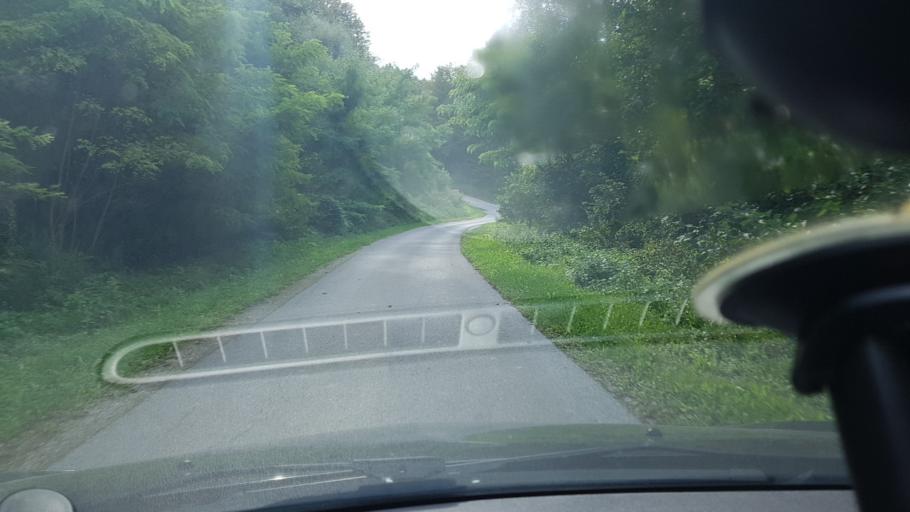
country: HR
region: Krapinsko-Zagorska
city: Radoboj
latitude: 46.1792
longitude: 15.9658
